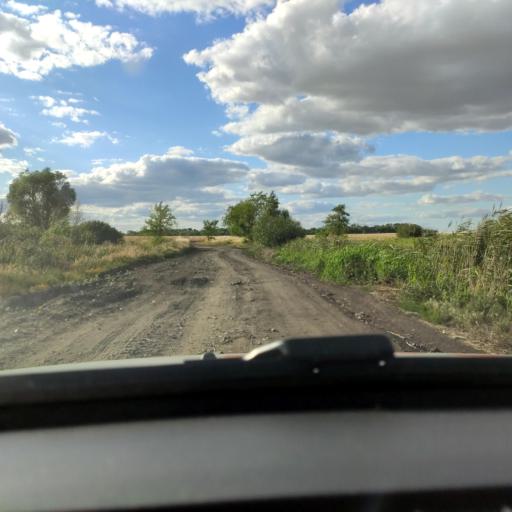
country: RU
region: Voronezj
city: Verkhnyaya Khava
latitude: 51.6073
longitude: 39.8361
